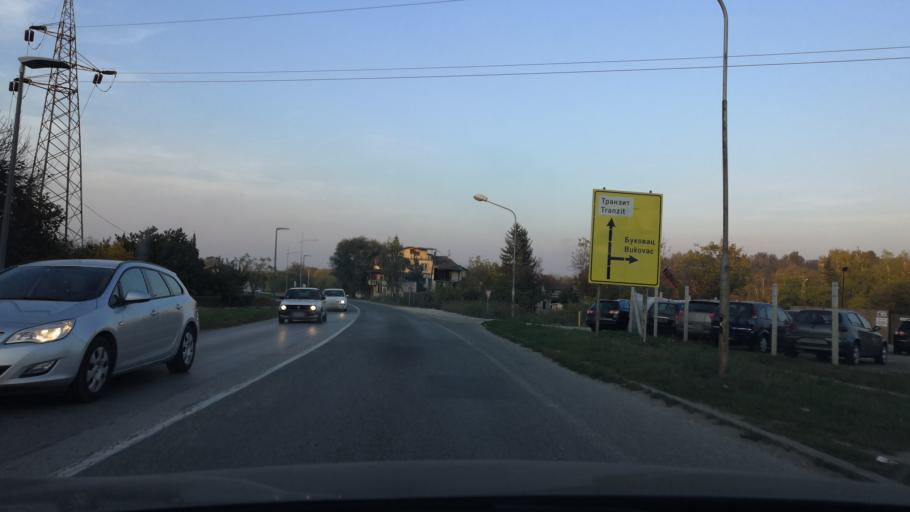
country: RS
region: Autonomna Pokrajina Vojvodina
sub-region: Juznobacki Okrug
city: Petrovaradin
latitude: 45.2302
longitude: 19.8834
